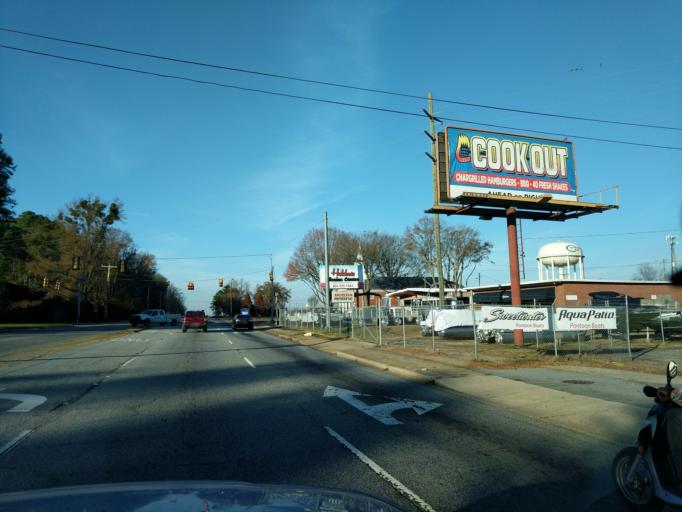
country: US
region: South Carolina
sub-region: Spartanburg County
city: Saxon
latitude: 34.9845
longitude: -81.9459
